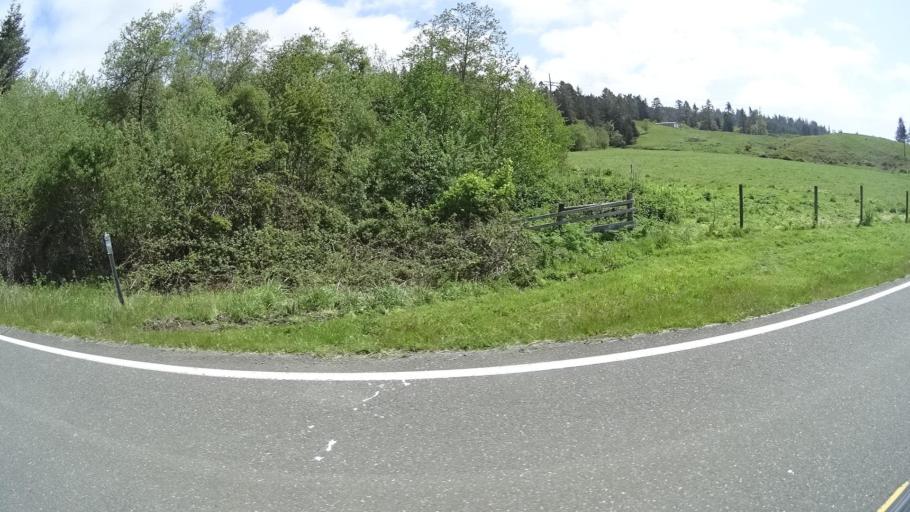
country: US
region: California
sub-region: Humboldt County
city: Humboldt Hill
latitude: 40.6754
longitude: -124.1973
